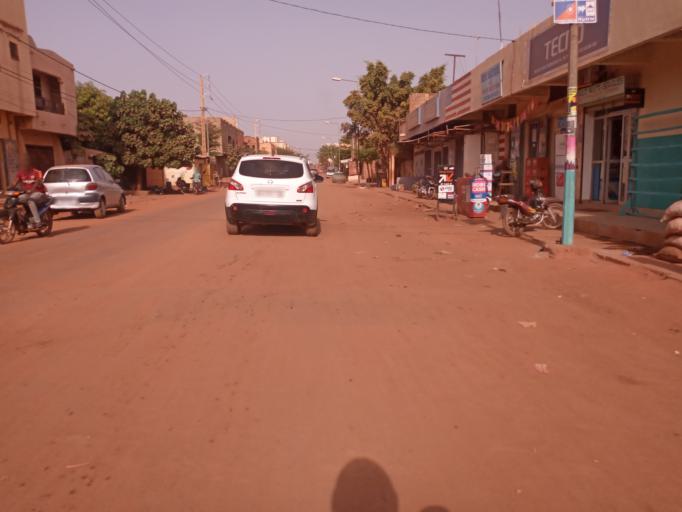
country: ML
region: Bamako
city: Bamako
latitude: 12.6797
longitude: -7.9420
